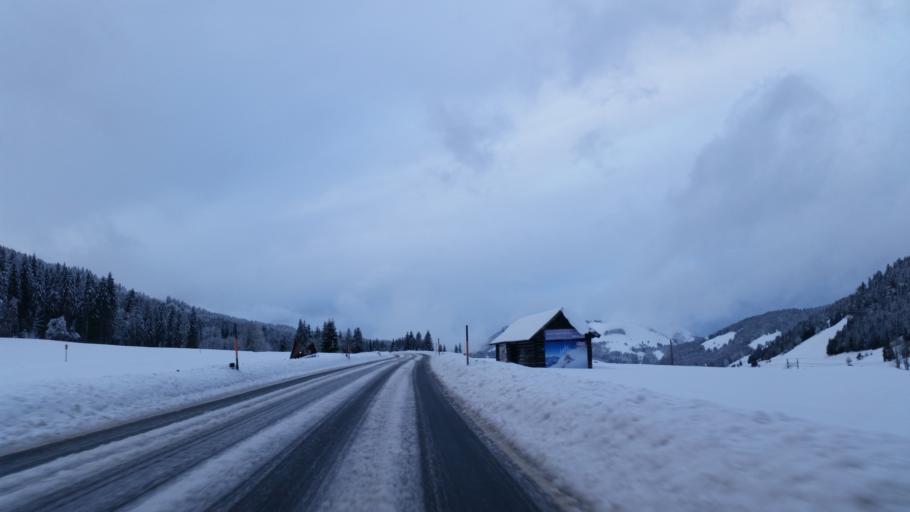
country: AT
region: Tyrol
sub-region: Politischer Bezirk Kitzbuhel
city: Hochfilzen
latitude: 47.4539
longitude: 12.6558
